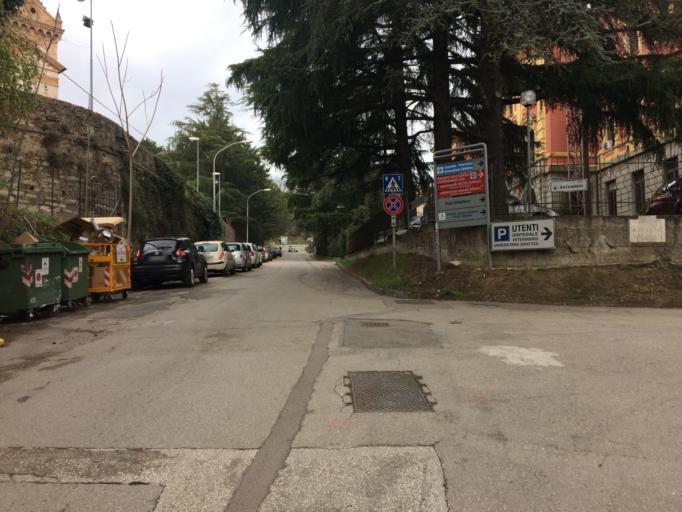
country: IT
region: Umbria
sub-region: Provincia di Perugia
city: Perugia
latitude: 43.0984
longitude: 12.3973
